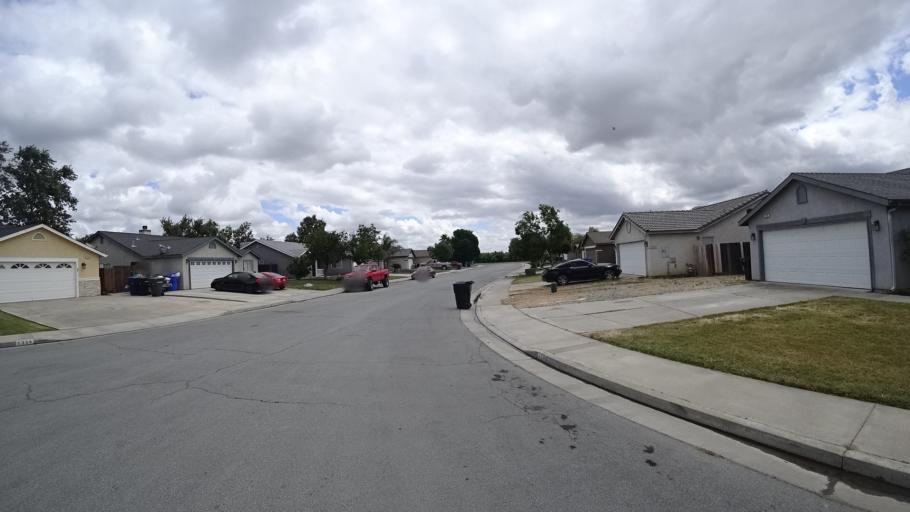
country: US
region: California
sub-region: Kings County
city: Hanford
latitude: 36.3347
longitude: -119.6249
